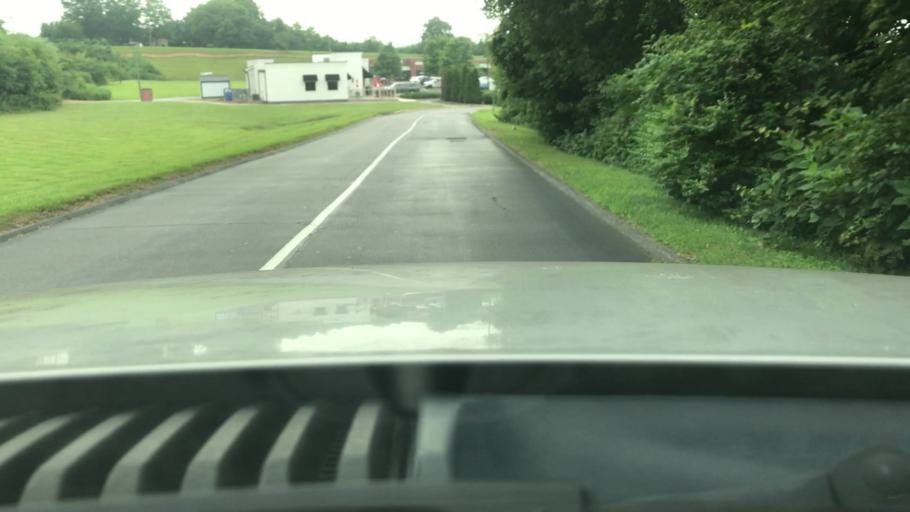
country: US
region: North Carolina
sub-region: Wilkes County
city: Wilkesboro
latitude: 36.1555
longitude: -81.1640
